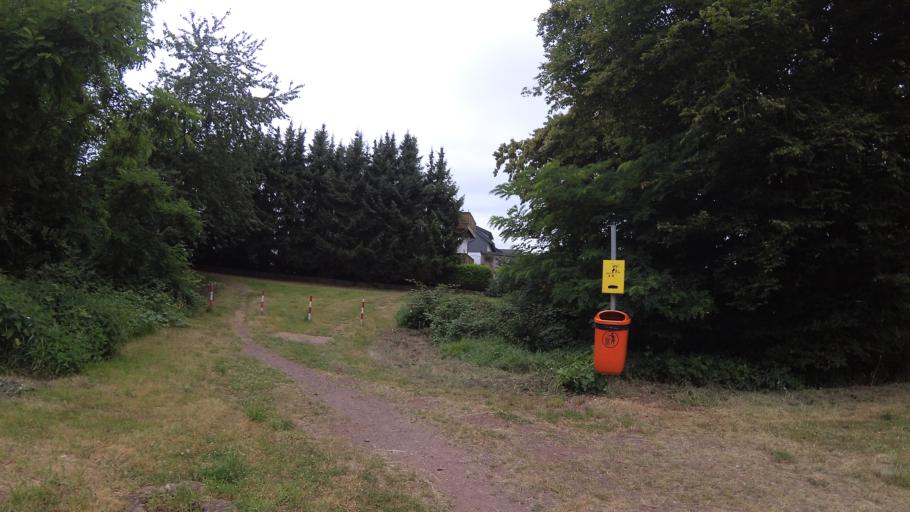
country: DE
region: Saarland
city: Schwalbach
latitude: 49.3122
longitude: 6.8110
